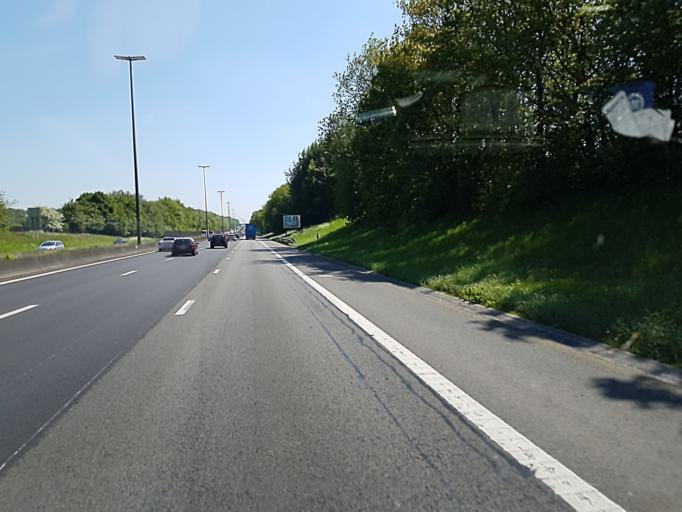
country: BE
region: Wallonia
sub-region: Province du Hainaut
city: Mons
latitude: 50.4889
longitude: 4.0110
